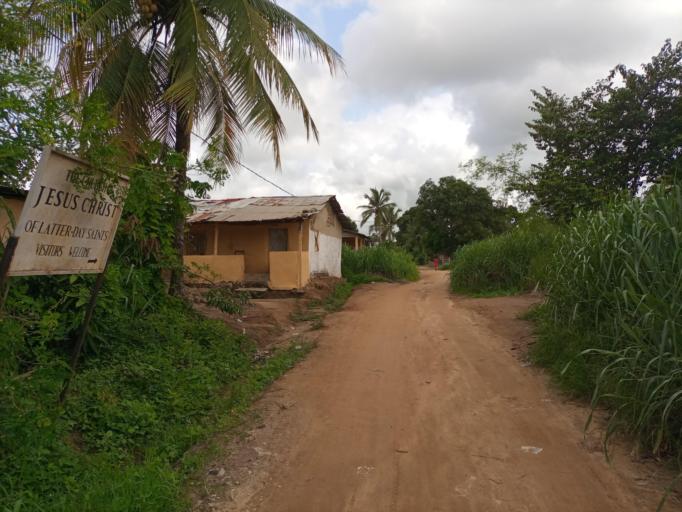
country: SL
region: Southern Province
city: Bo
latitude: 7.9626
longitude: -11.7584
